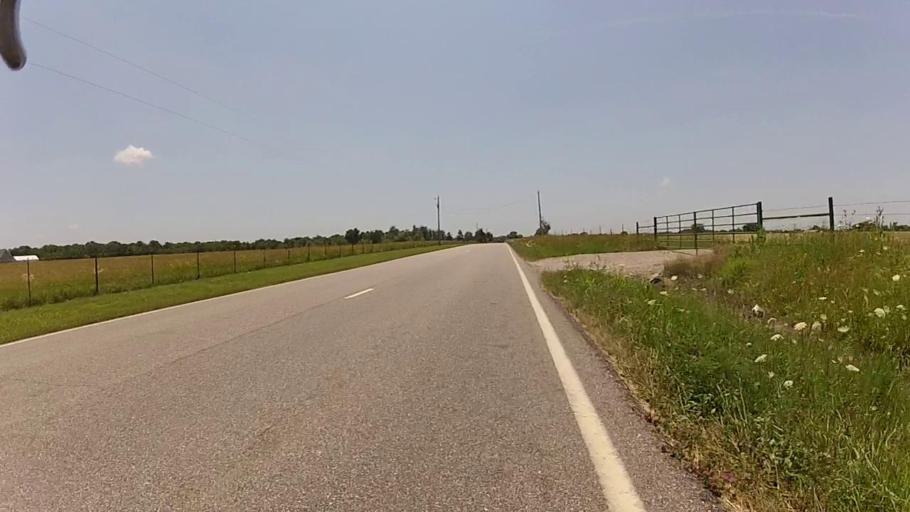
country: US
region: Kansas
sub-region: Montgomery County
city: Cherryvale
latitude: 37.2256
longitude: -95.5381
